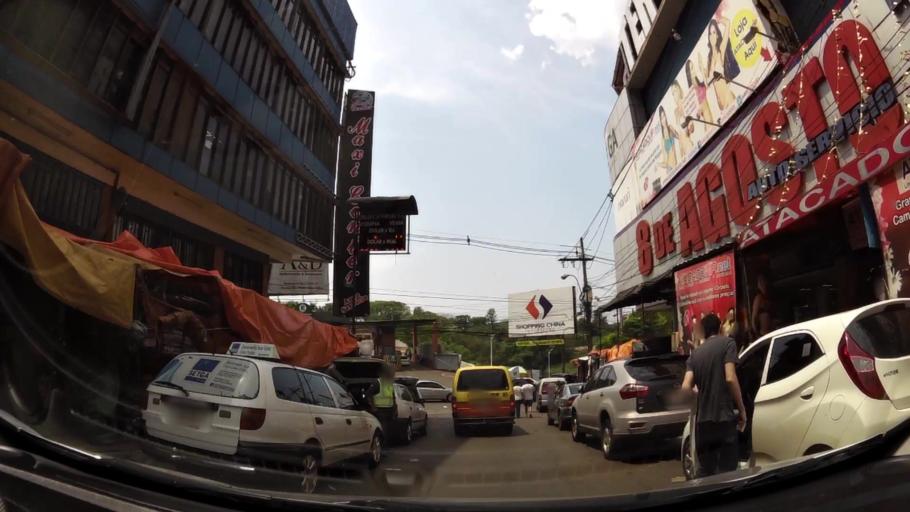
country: PY
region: Alto Parana
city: Ciudad del Este
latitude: -25.5114
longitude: -54.6074
